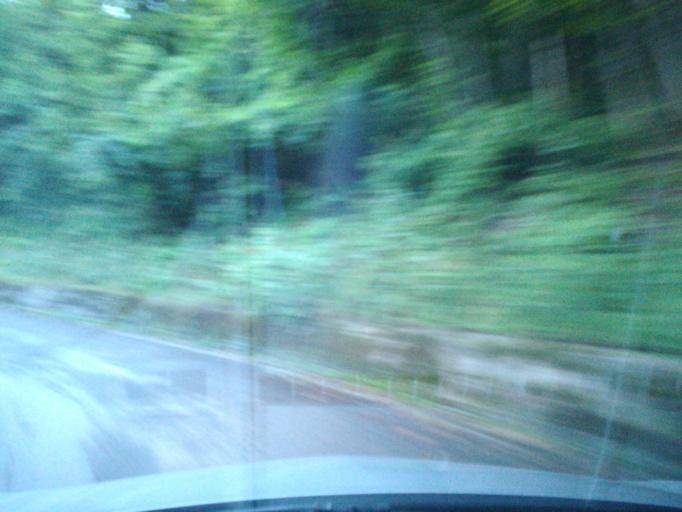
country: IT
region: Lombardy
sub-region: Provincia di Bergamo
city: Valsecca
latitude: 45.8131
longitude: 9.4909
